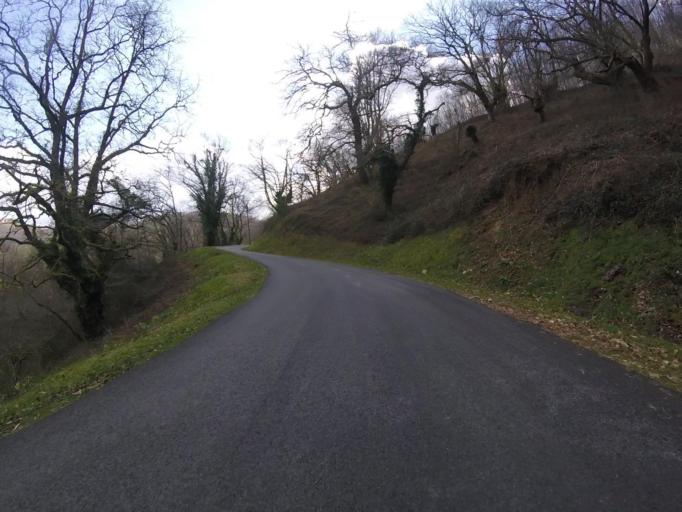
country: ES
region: Navarre
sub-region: Provincia de Navarra
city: Etxalar
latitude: 43.2609
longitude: -1.6157
